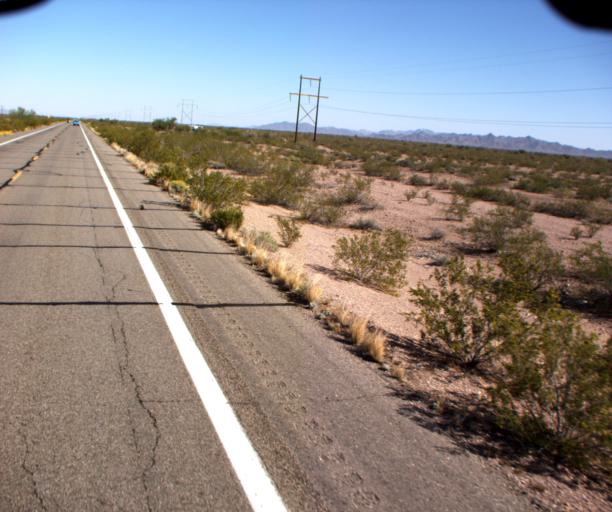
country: US
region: Arizona
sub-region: La Paz County
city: Quartzsite
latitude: 33.3846
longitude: -114.2171
